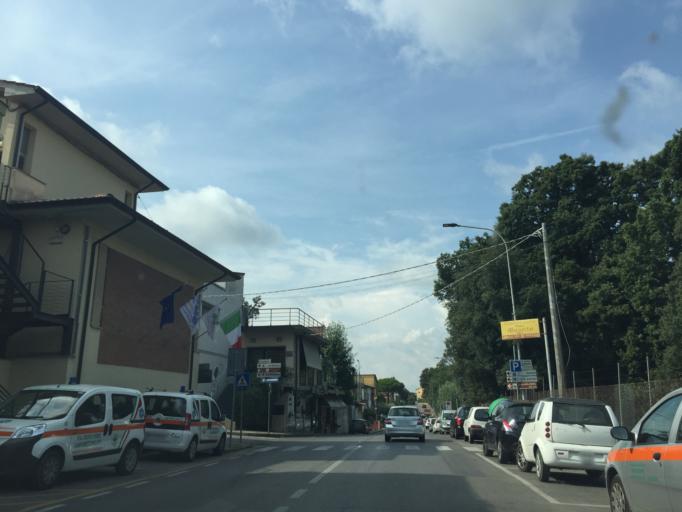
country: IT
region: Tuscany
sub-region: Provincia di Pistoia
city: Larciano
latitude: 43.8155
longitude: 10.8948
